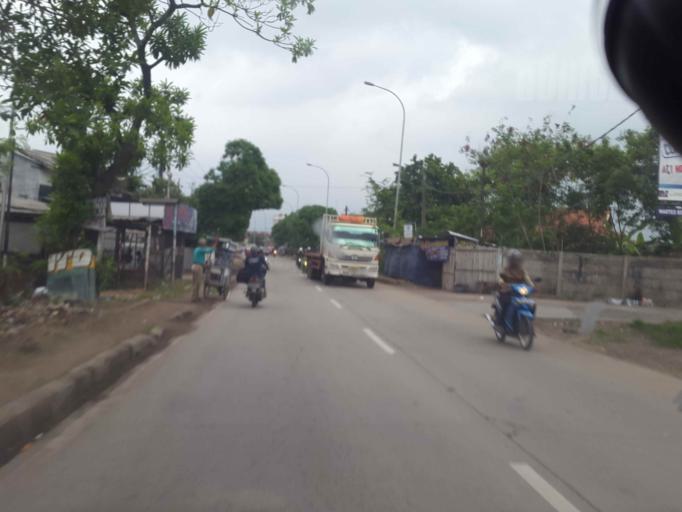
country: ID
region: West Java
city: Cikarang
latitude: -6.2846
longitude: 107.1605
